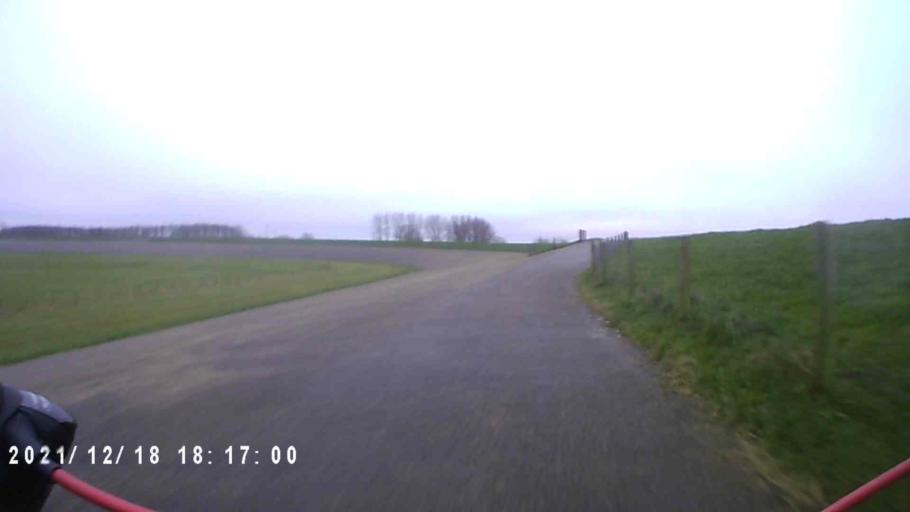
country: NL
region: Friesland
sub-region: Gemeente Dongeradeel
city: Ternaard
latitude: 53.3933
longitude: 5.9703
